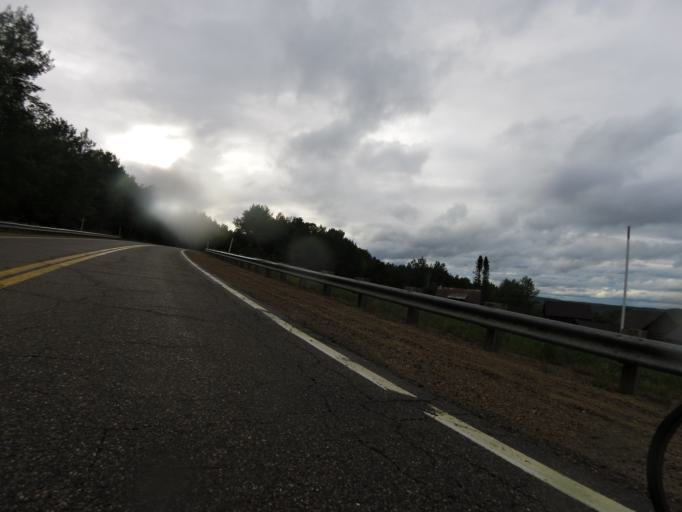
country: CA
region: Quebec
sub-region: Outaouais
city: Shawville
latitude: 45.9055
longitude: -76.2769
